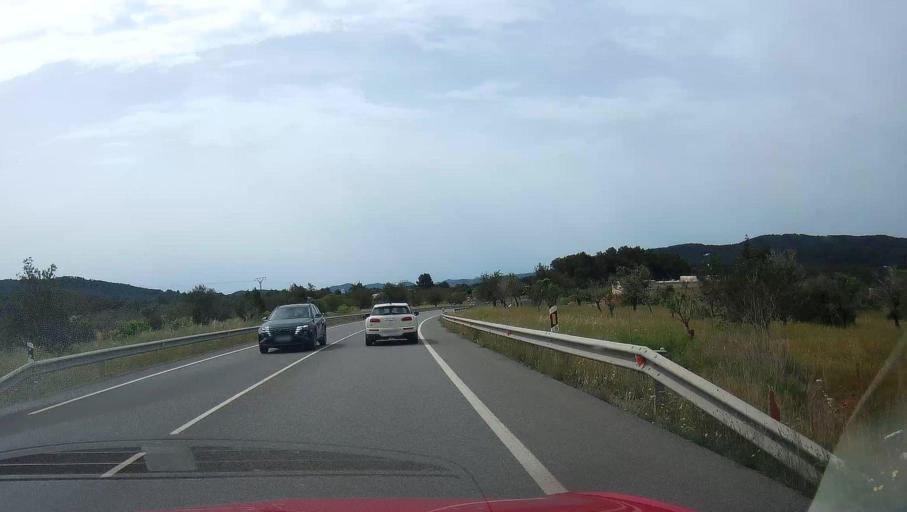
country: ES
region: Balearic Islands
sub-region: Illes Balears
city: Sant Joan de Labritja
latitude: 39.0629
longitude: 1.4948
